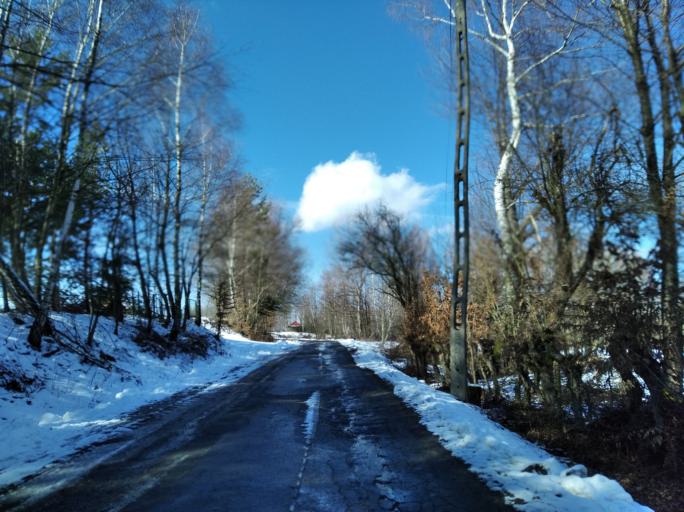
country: PL
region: Subcarpathian Voivodeship
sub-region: Powiat brzozowski
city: Jablonica Polska
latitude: 49.7292
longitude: 21.8698
